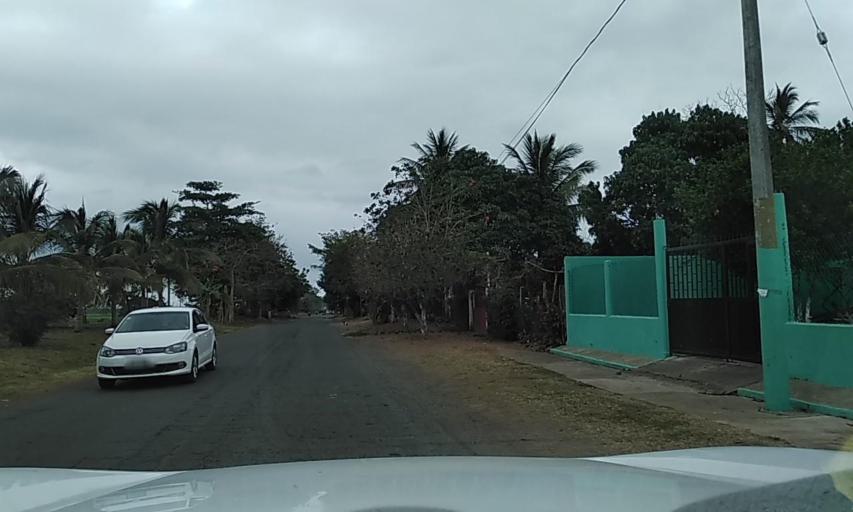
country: MX
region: Veracruz
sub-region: Veracruz
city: Delfino Victoria (Santa Fe)
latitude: 19.2659
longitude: -96.3192
